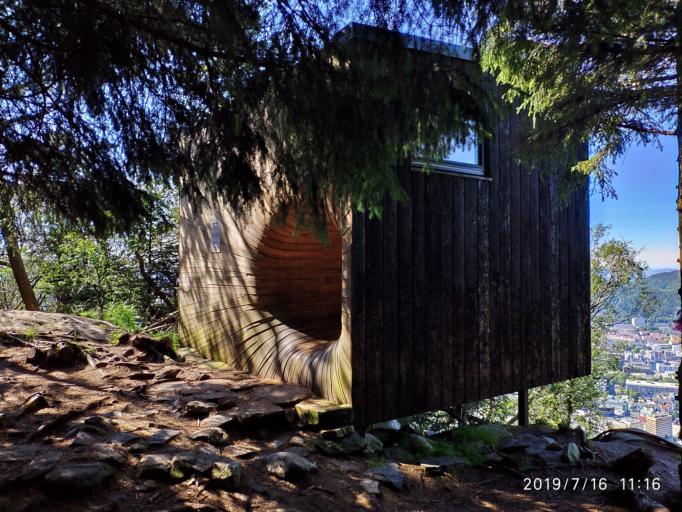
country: NO
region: Hordaland
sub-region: Bergen
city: Bergen
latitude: 60.3929
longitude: 5.3455
